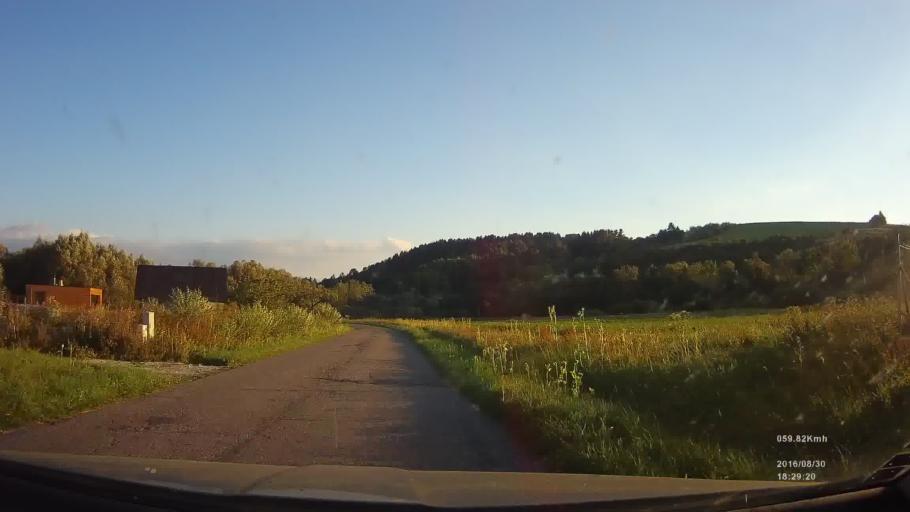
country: SK
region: Zilinsky
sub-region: Okres Liptovsky Mikulas
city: Liptovsky Mikulas
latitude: 49.1334
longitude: 19.5017
